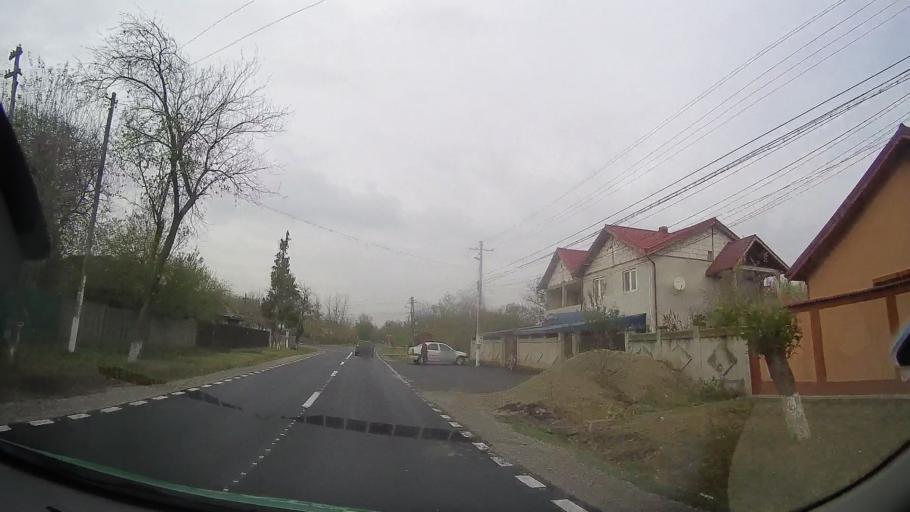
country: RO
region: Ilfov
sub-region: Comuna Nuci
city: Nuci
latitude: 44.7203
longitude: 26.3041
